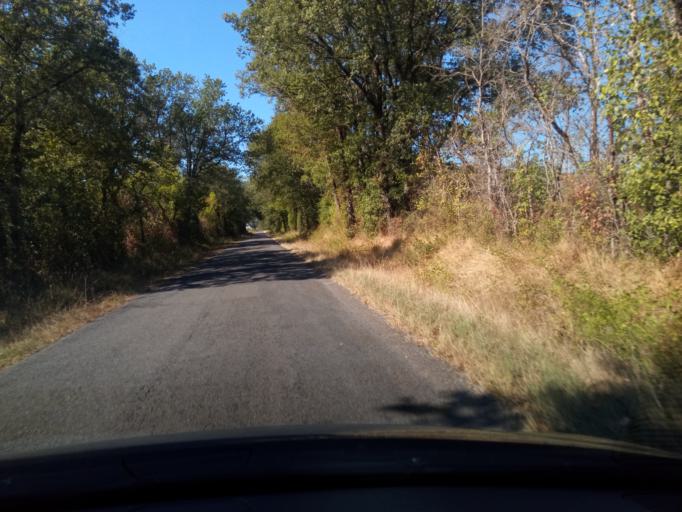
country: FR
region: Poitou-Charentes
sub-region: Departement de la Vienne
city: Montmorillon
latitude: 46.4807
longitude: 0.8899
